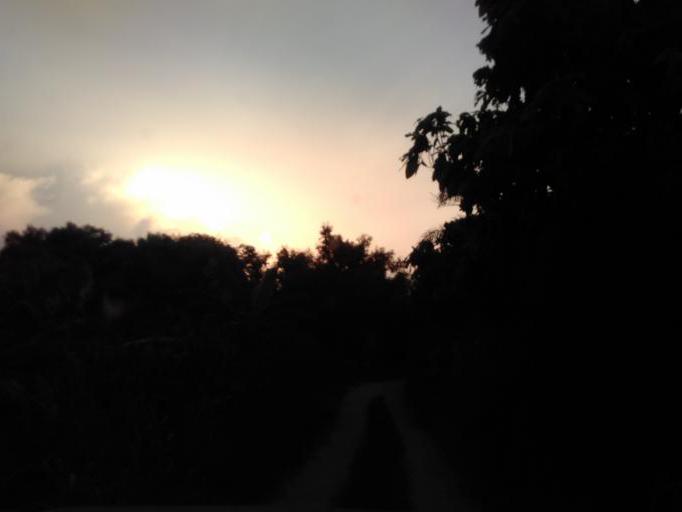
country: GH
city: Bekwai
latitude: 6.5263
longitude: -1.4384
